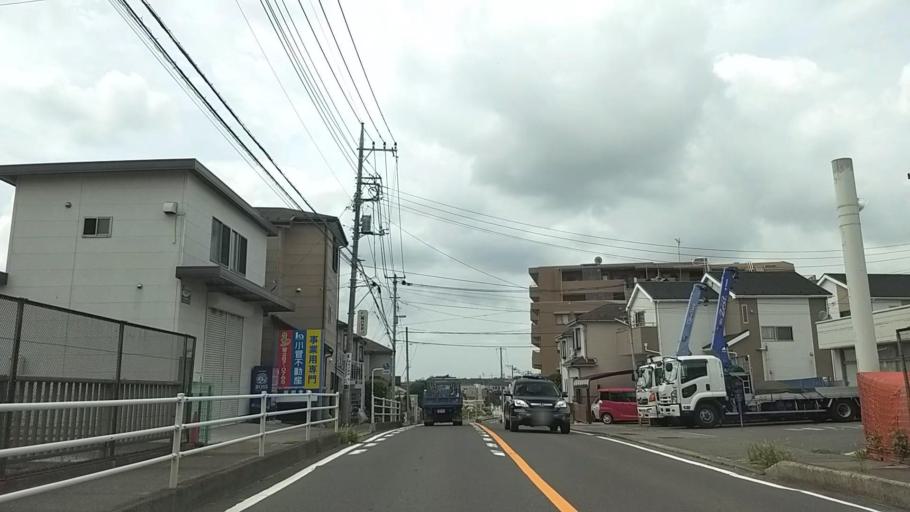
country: JP
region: Kanagawa
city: Minami-rinkan
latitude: 35.4417
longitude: 139.4592
